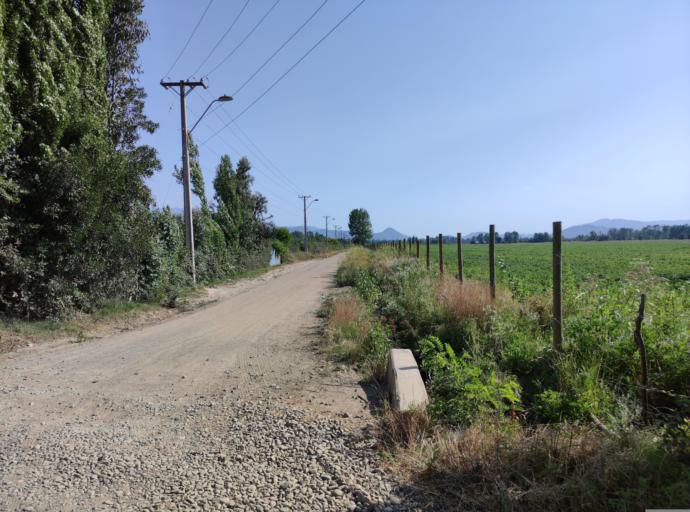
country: CL
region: O'Higgins
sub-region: Provincia de Cachapoal
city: Rengo
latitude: -34.3485
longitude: -70.8263
